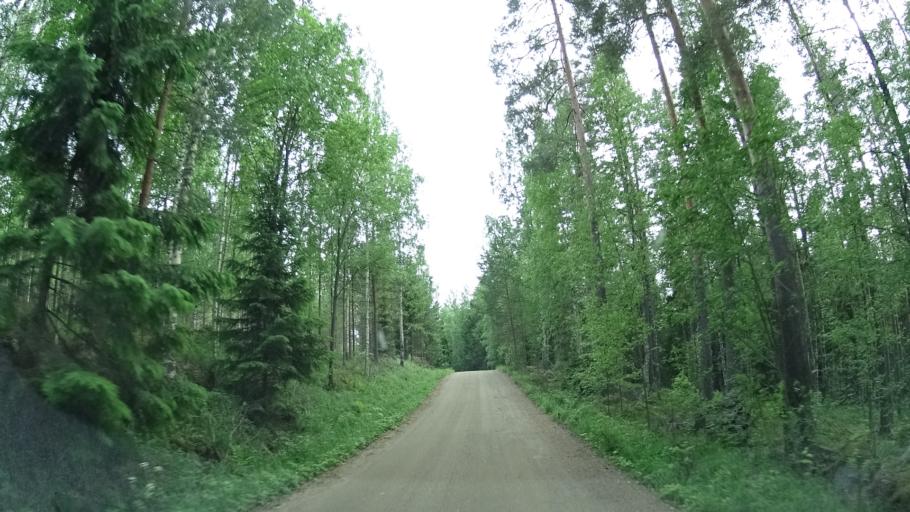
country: FI
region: Central Finland
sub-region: Joutsa
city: Luhanka
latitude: 61.6848
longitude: 25.6875
